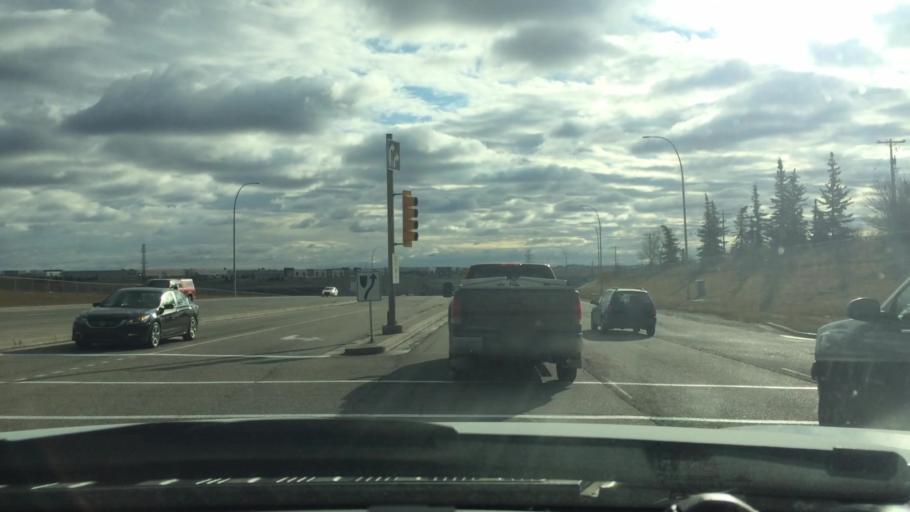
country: CA
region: Alberta
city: Calgary
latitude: 51.1278
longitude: -114.0531
